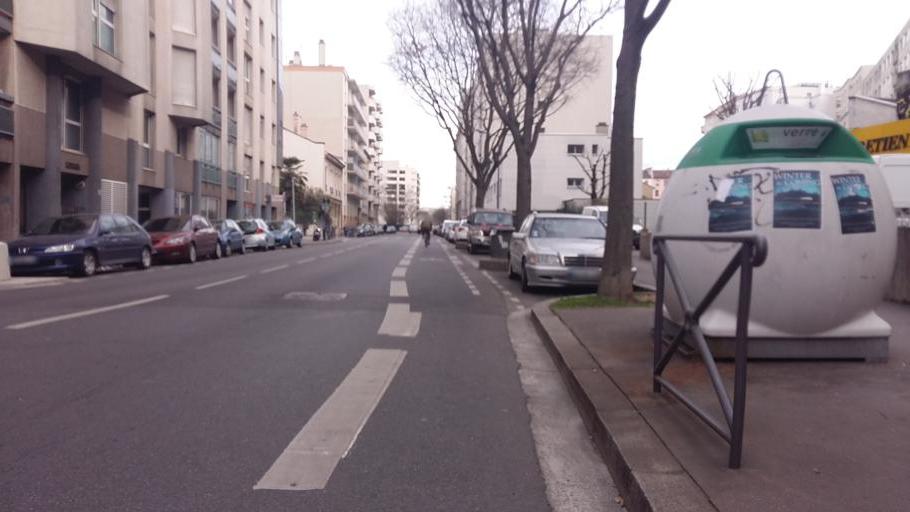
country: FR
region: Rhone-Alpes
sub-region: Departement du Rhone
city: Villeurbanne
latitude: 45.7717
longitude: 4.8703
